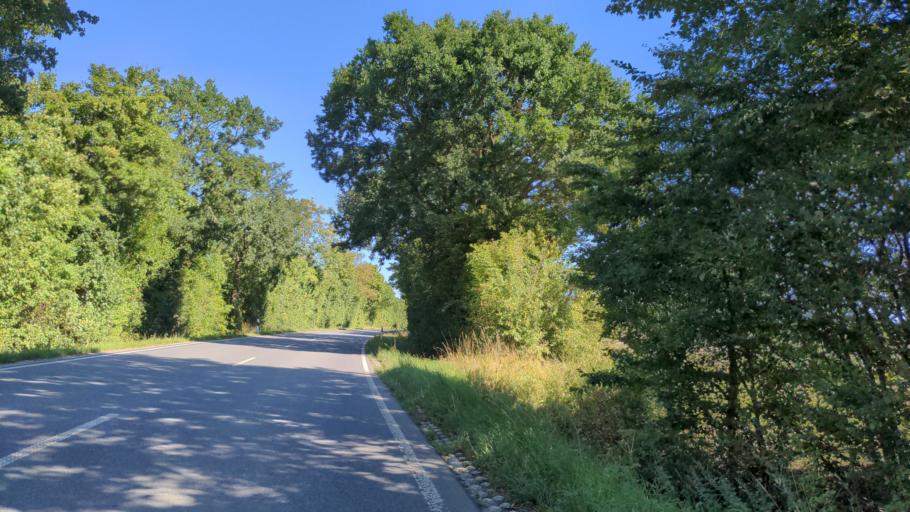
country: DE
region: Schleswig-Holstein
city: Grinau
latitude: 53.7888
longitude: 10.5606
